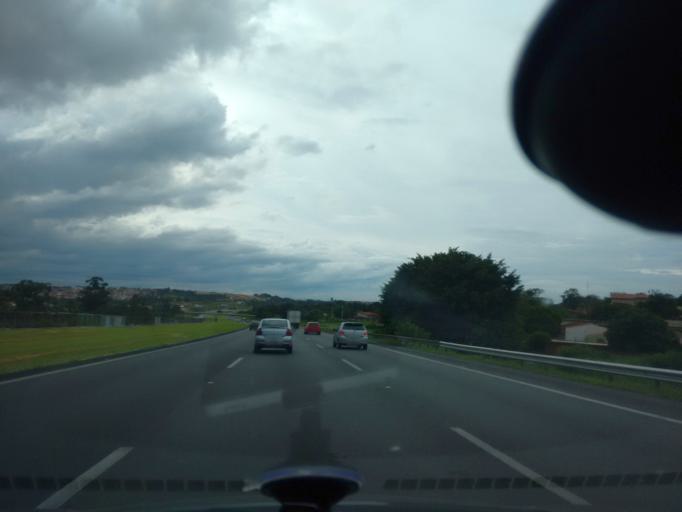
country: BR
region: Sao Paulo
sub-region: Campinas
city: Campinas
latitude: -22.9695
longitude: -47.1170
